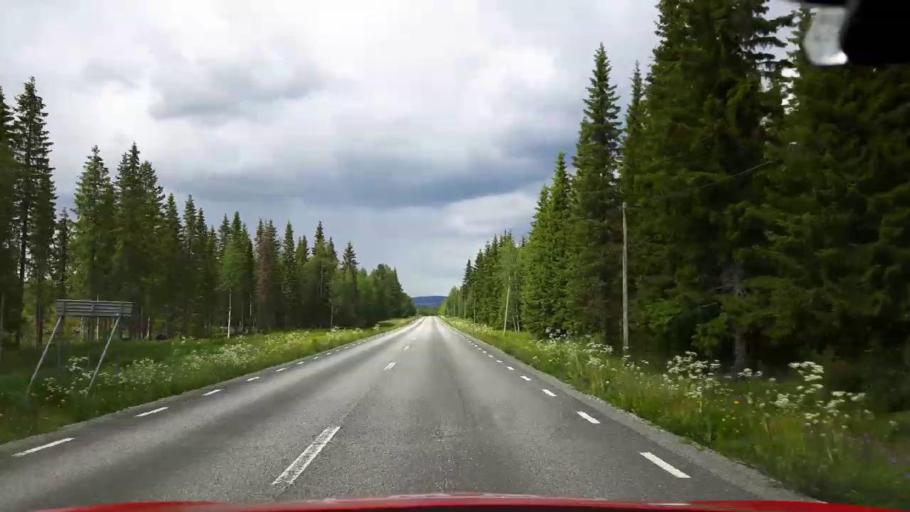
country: SE
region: Jaemtland
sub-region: Krokoms Kommun
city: Krokom
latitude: 63.6492
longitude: 14.3779
